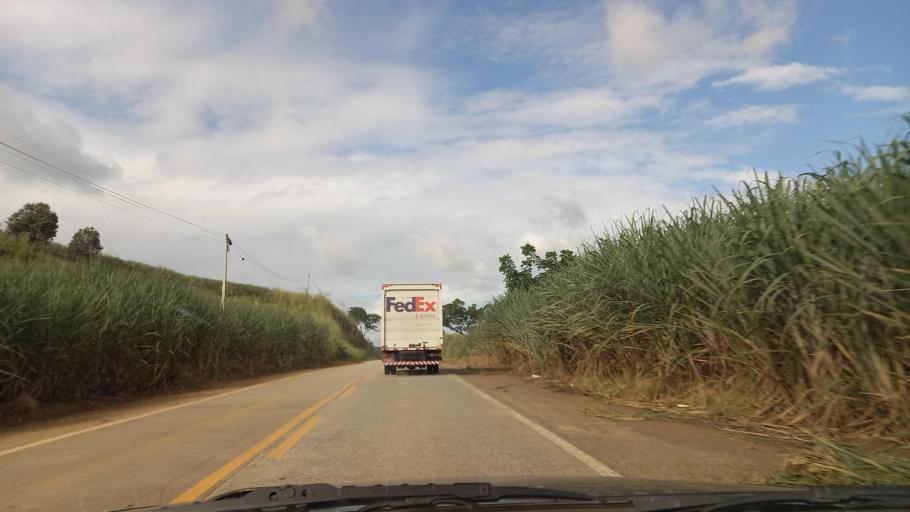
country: BR
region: Pernambuco
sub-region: Palmares
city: Palmares
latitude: -8.6942
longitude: -35.6454
